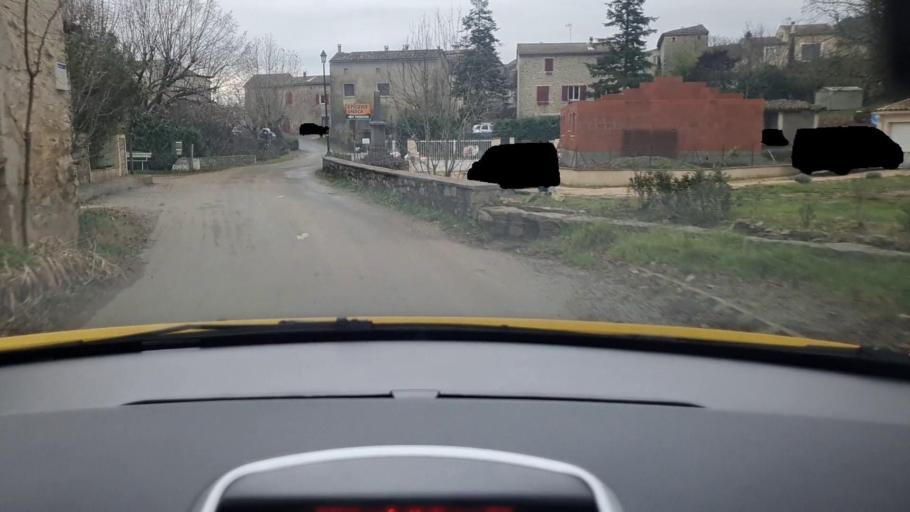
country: FR
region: Languedoc-Roussillon
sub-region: Departement du Gard
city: Molieres-sur-Ceze
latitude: 44.2997
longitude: 4.1545
